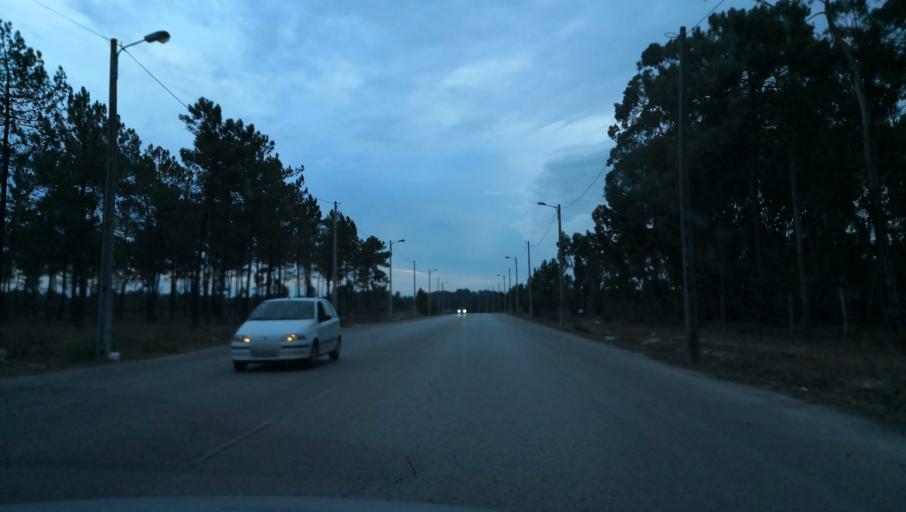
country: PT
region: Setubal
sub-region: Almada
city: Charneca
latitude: 38.5991
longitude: -9.1610
